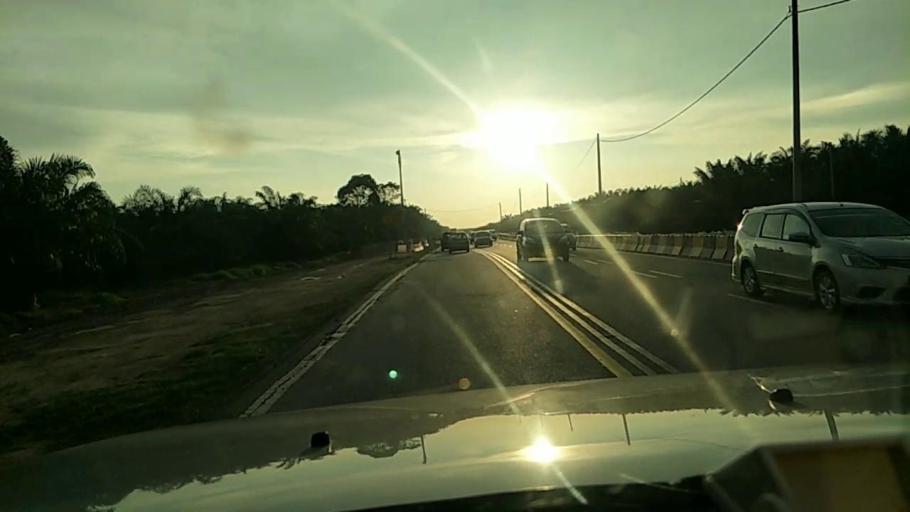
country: MY
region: Perak
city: Kampong Dungun
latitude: 3.3062
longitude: 101.3466
